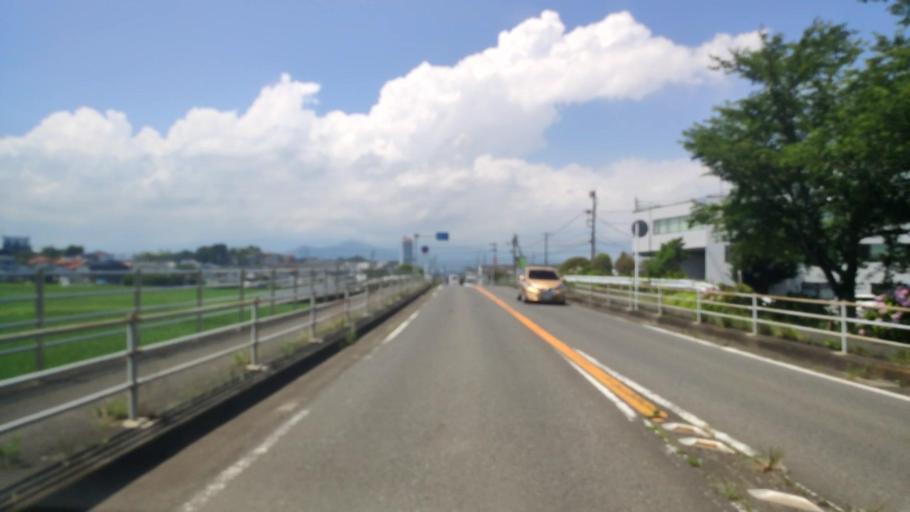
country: JP
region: Kanagawa
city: Oiso
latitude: 35.3430
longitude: 139.3069
